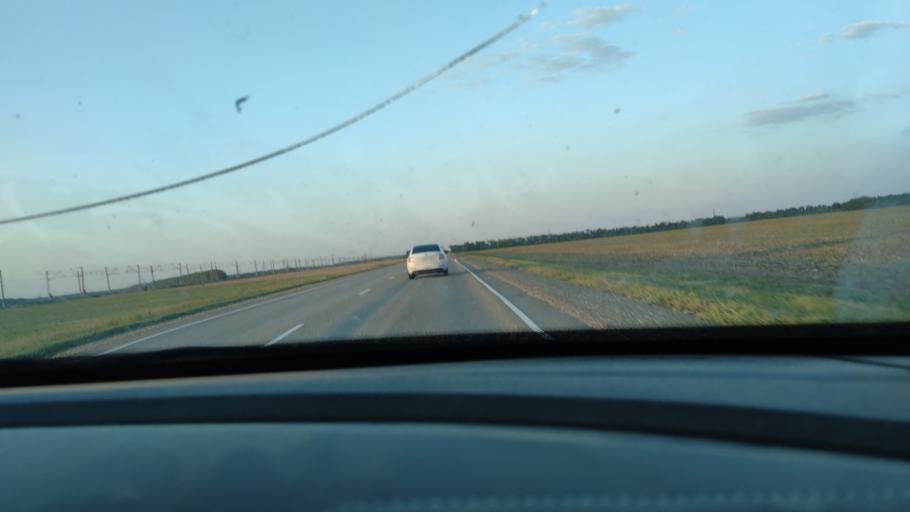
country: RU
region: Krasnodarskiy
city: Novominskaya
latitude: 46.3827
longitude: 38.9841
